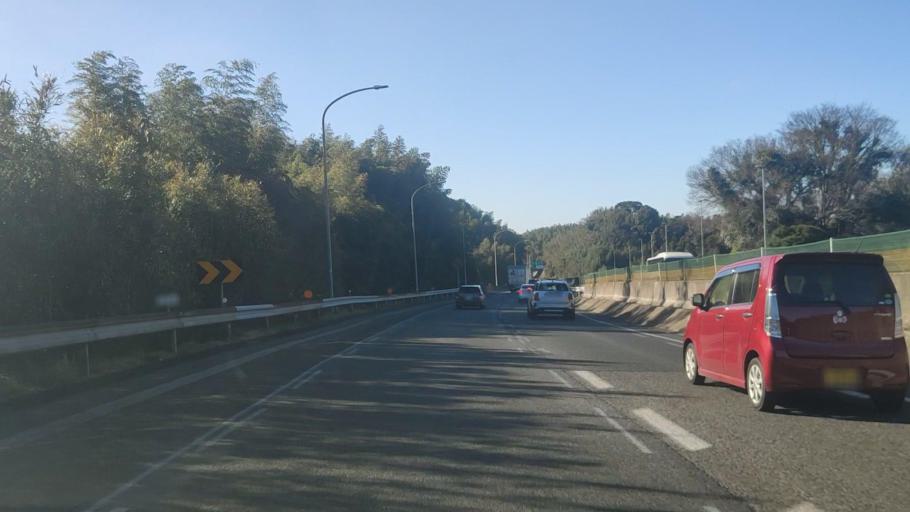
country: JP
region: Fukuoka
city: Nishifukuma
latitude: 33.7499
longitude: 130.5433
